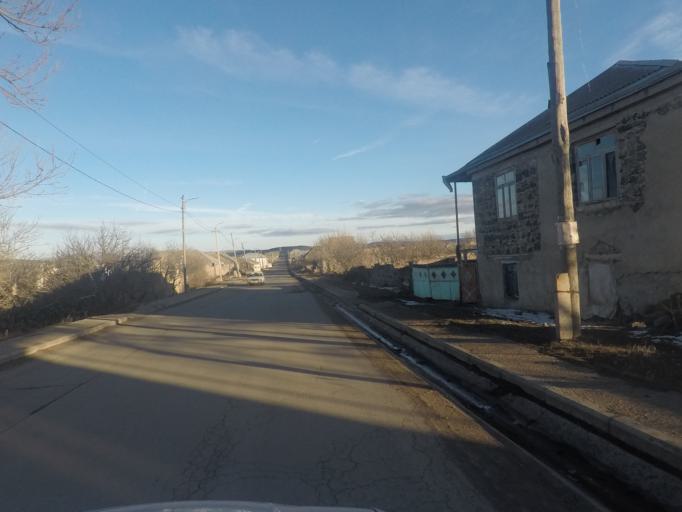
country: GE
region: Kvemo Kartli
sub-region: Tsalka
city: Tsalka
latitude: 41.6056
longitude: 44.0423
